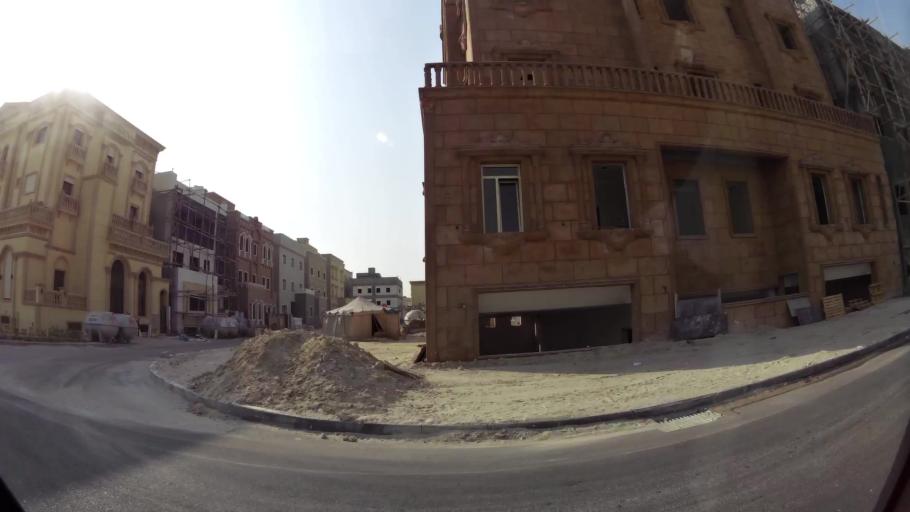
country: KW
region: Al Asimah
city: Ar Rabiyah
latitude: 29.3310
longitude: 47.8038
